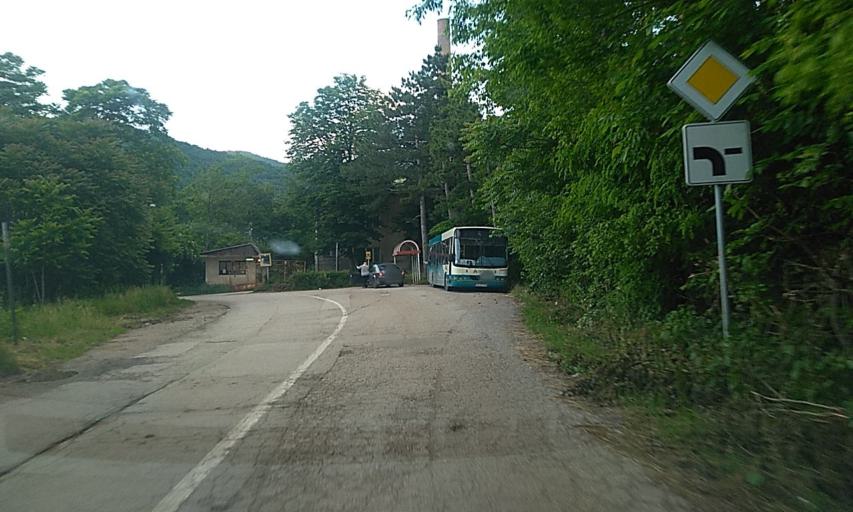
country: RS
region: Central Serbia
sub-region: Nisavski Okrug
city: Niska Banja
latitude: 43.3690
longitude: 21.9881
